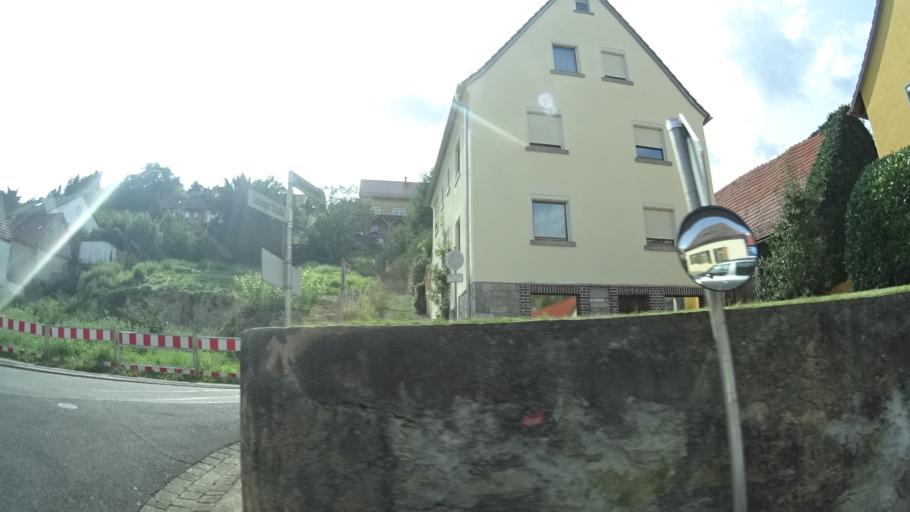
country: DE
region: Bavaria
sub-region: Regierungsbezirk Unterfranken
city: Zellingen
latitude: 49.8686
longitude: 9.7991
